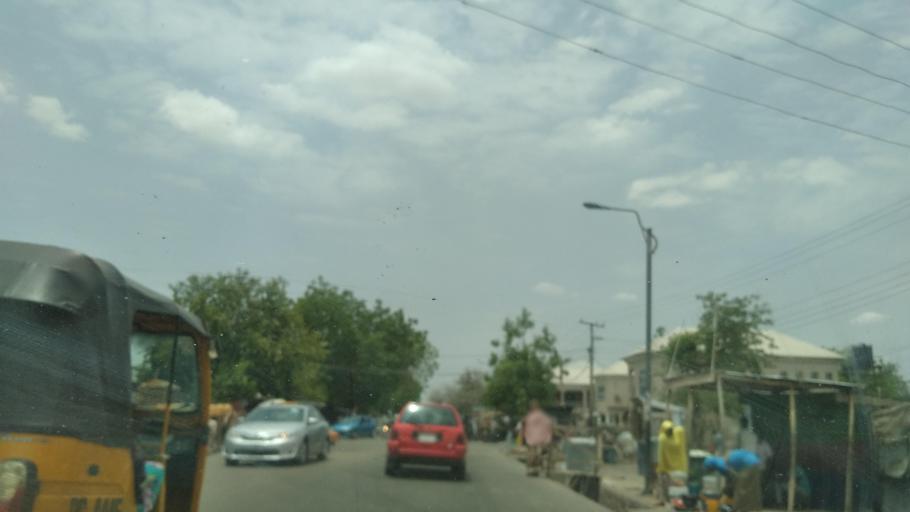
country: NG
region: Borno
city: Maiduguri
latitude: 11.8067
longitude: 13.1622
